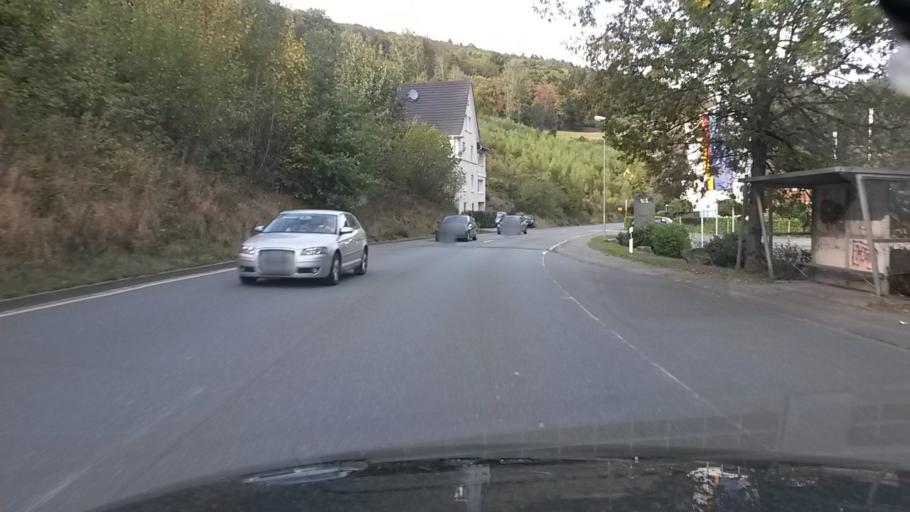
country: DE
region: North Rhine-Westphalia
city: Altena
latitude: 51.2350
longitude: 7.6978
